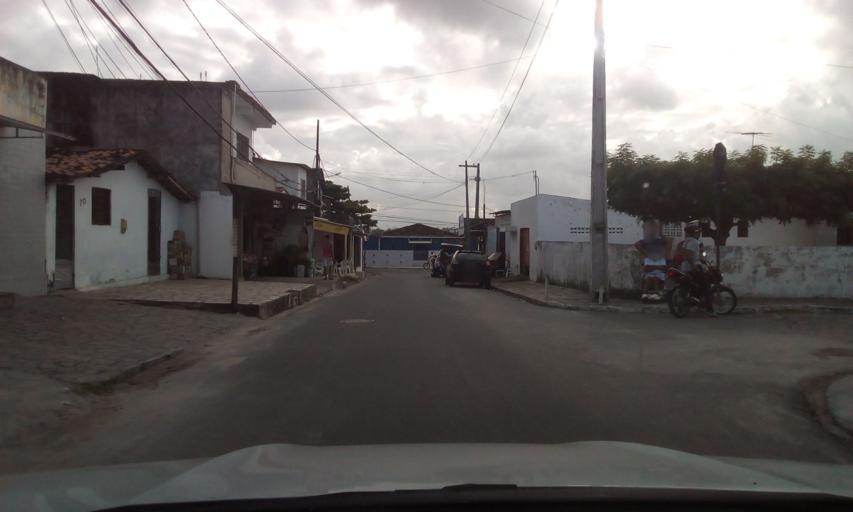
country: BR
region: Paraiba
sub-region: Joao Pessoa
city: Joao Pessoa
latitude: -7.1639
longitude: -34.8415
